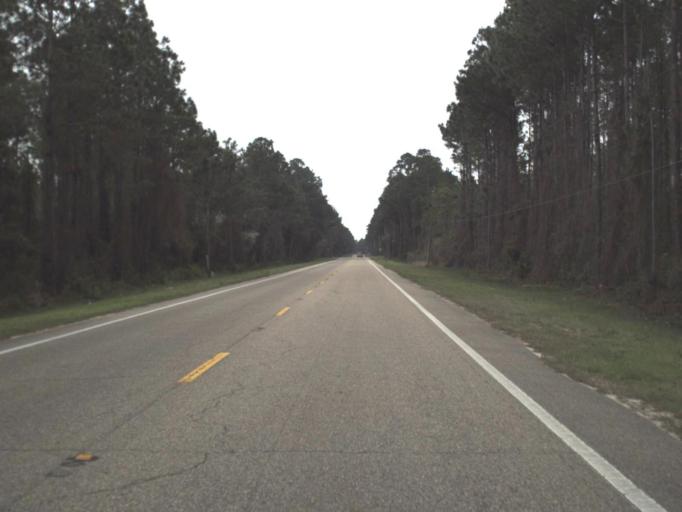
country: US
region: Florida
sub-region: Gulf County
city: Port Saint Joe
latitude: 29.8306
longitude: -85.2775
